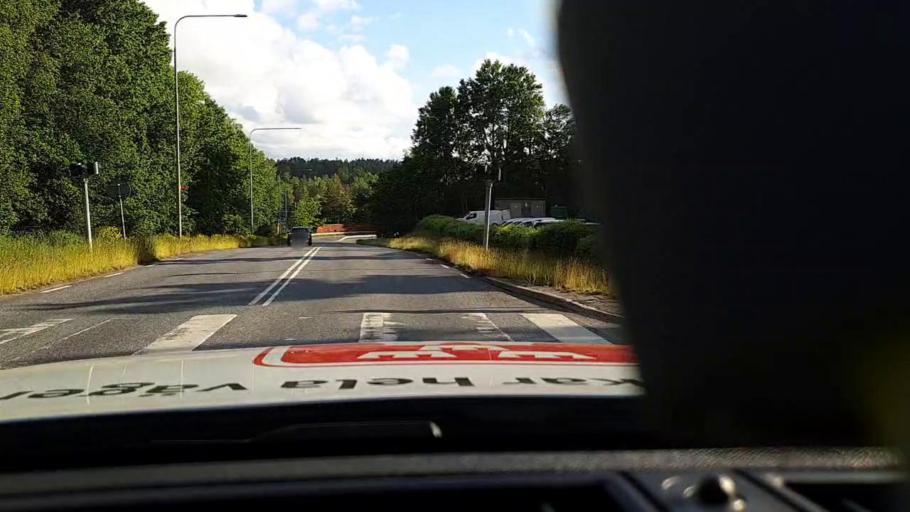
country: SE
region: Stockholm
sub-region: Huddinge Kommun
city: Huddinge
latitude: 59.2515
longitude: 17.9669
